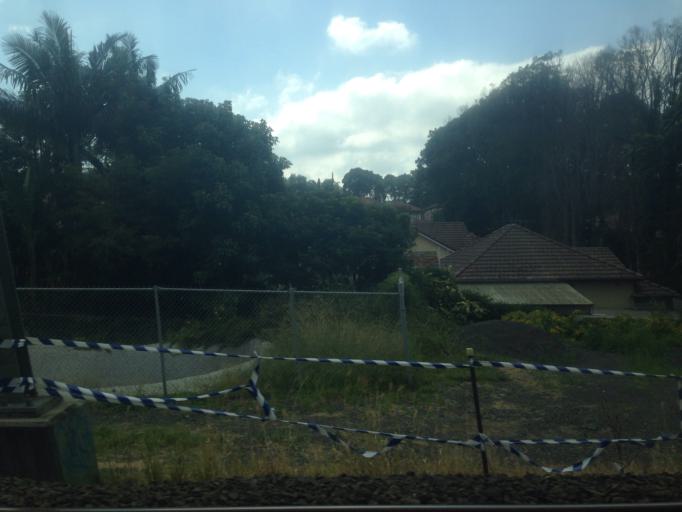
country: AU
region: New South Wales
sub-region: Willoughby
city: Chatswood
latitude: -33.8063
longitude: 151.1825
